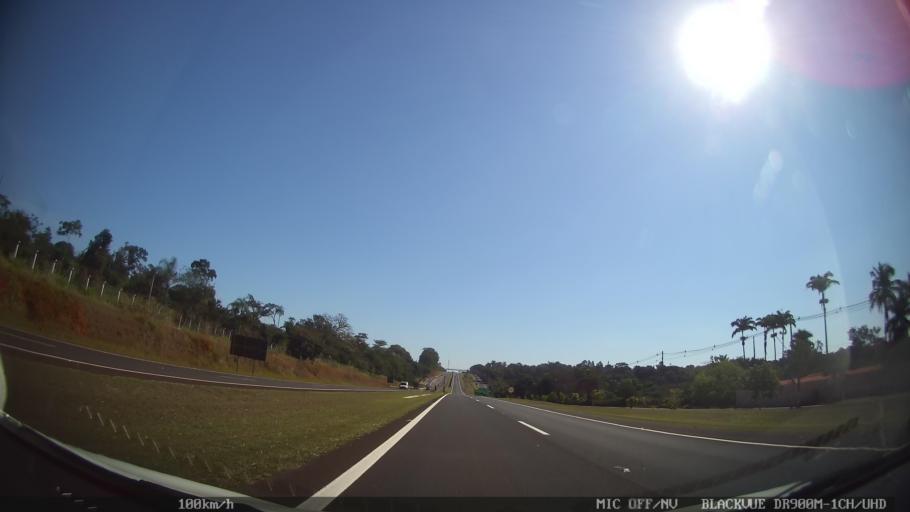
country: BR
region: Sao Paulo
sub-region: Ribeirao Preto
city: Ribeirao Preto
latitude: -21.2131
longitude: -47.8425
